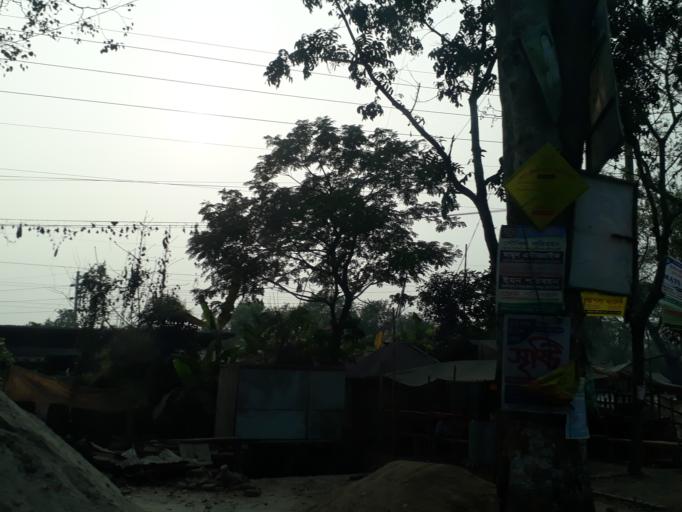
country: BD
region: Khulna
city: Bhatpara Abhaynagar
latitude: 22.9352
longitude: 89.4882
